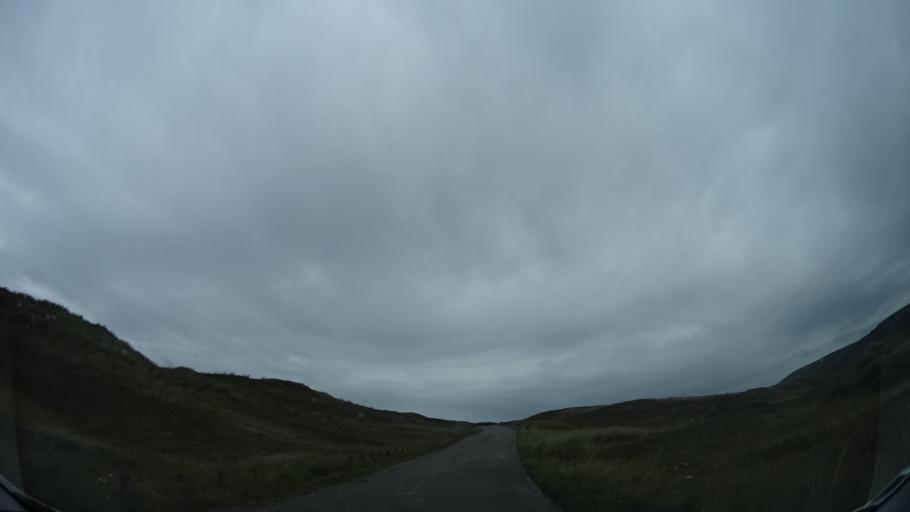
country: FR
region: Lower Normandy
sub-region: Departement de la Manche
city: Beaumont-Hague
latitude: 49.6080
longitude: -1.8382
